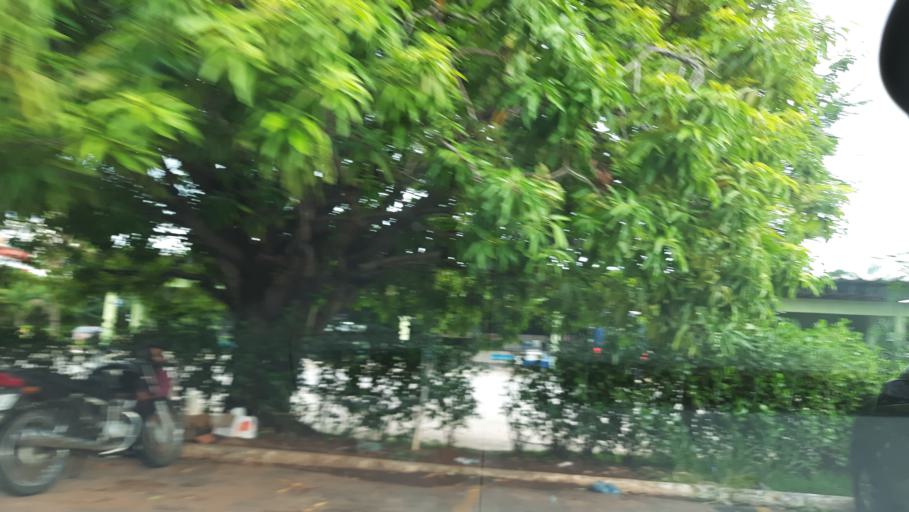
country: BR
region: Sao Paulo
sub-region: Sao Joao Da Boa Vista
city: Sao Joao da Boa Vista
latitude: -21.9889
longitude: -46.7929
